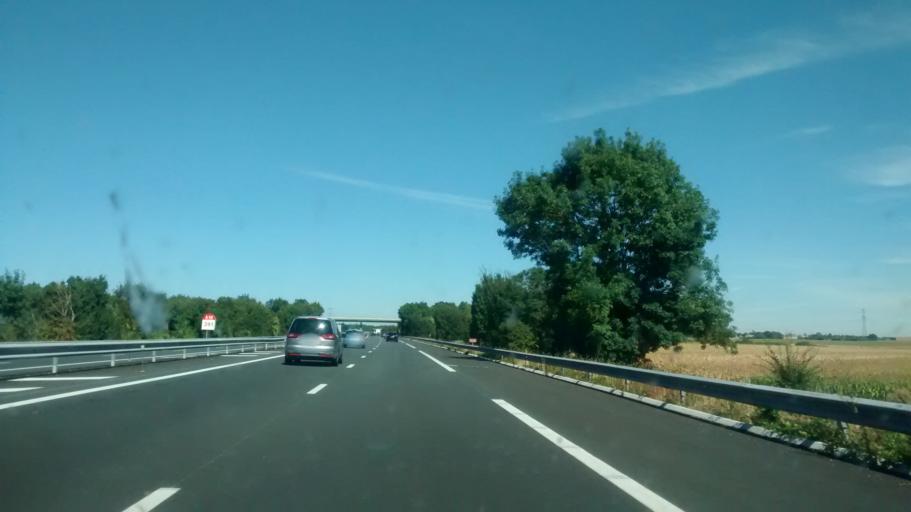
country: FR
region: Poitou-Charentes
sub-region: Departement des Deux-Sevres
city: Beauvoir-sur-Niort
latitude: 46.1557
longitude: -0.5171
